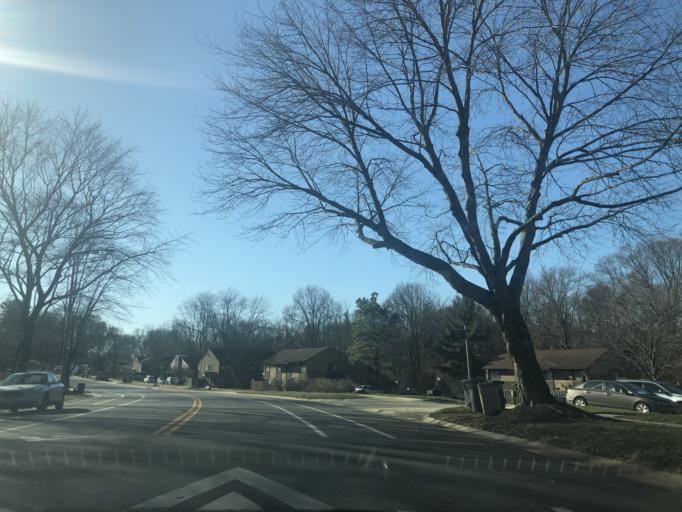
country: US
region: Maryland
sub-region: Howard County
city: Columbia
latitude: 39.2143
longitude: -76.8413
